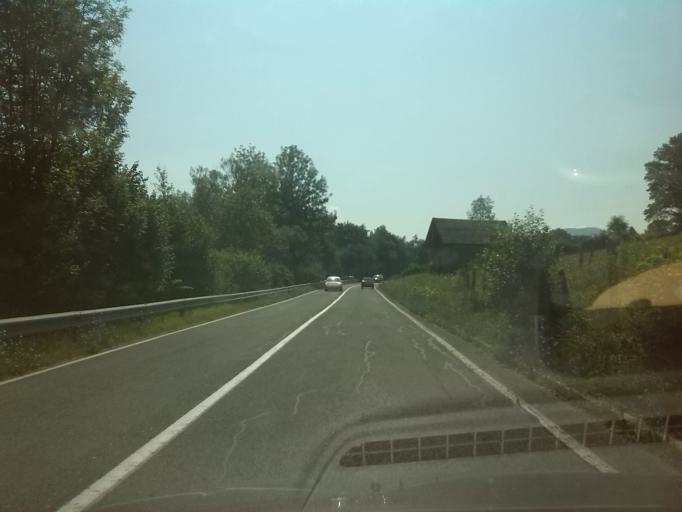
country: SI
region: Tolmin
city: Tolmin
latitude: 46.1996
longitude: 13.6886
